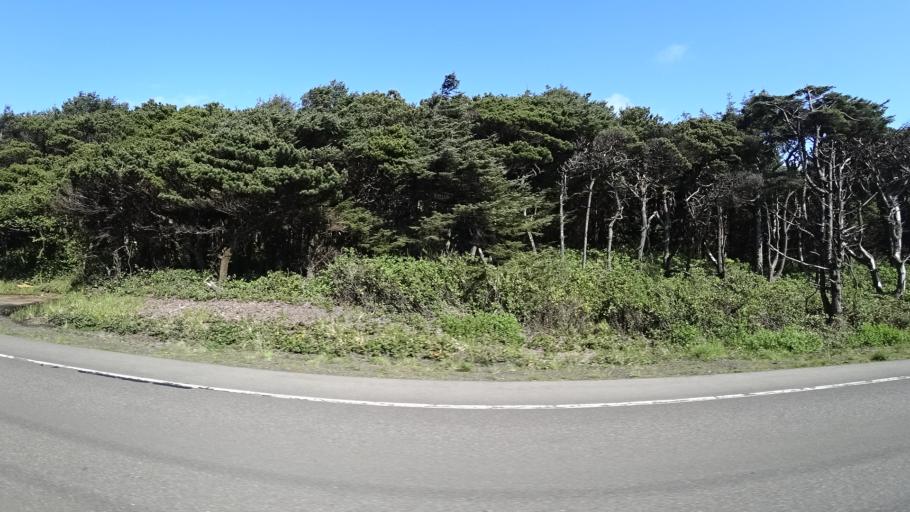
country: US
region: Oregon
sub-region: Lincoln County
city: Newport
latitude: 44.5599
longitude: -124.0705
